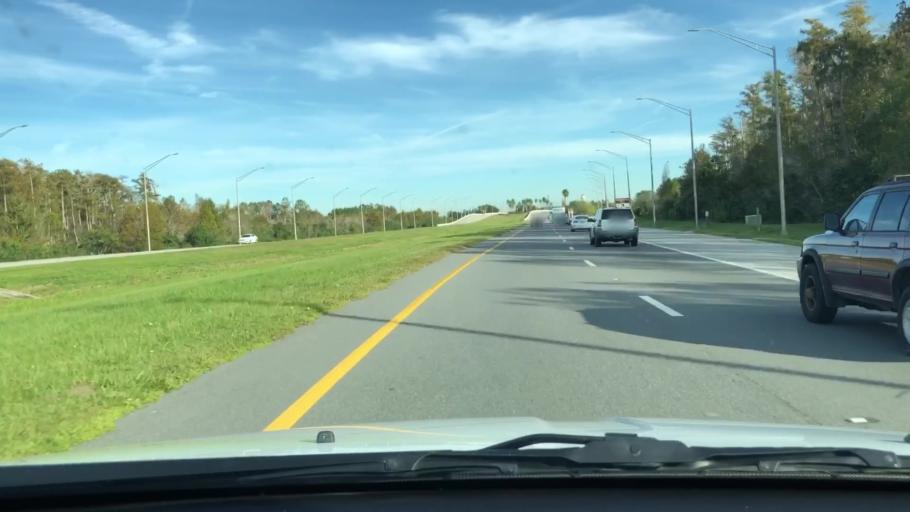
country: US
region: Florida
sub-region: Orange County
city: Meadow Woods
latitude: 28.3905
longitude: -81.3100
